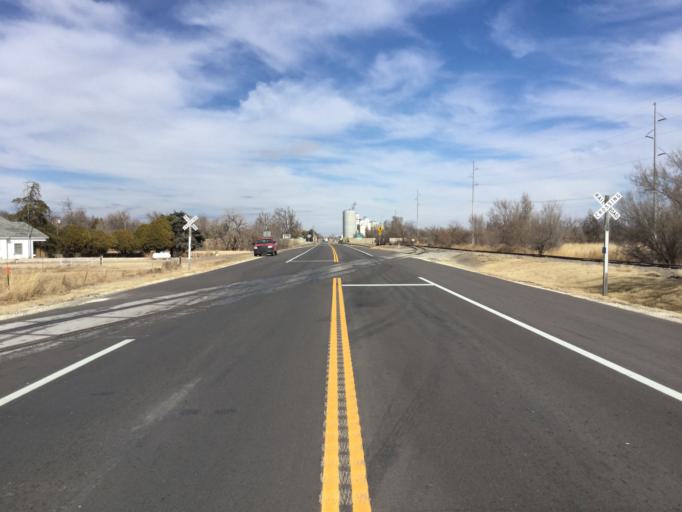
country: US
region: Kansas
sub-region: Pawnee County
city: Larned
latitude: 38.1702
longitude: -99.1070
